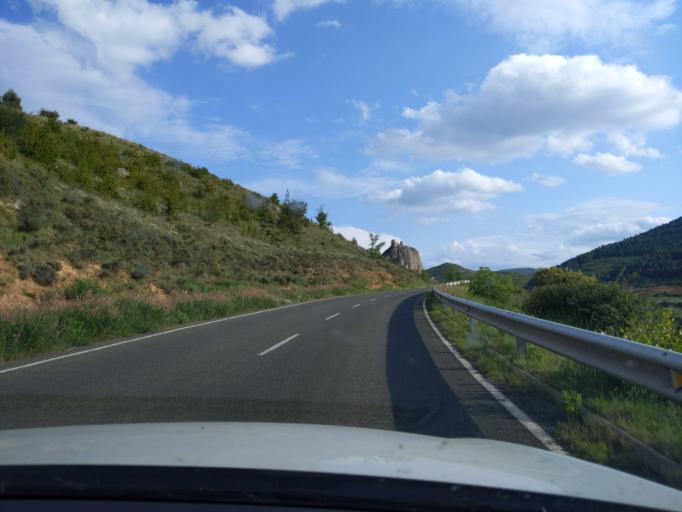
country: ES
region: La Rioja
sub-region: Provincia de La Rioja
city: Clavijo
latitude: 42.3581
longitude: -2.4262
